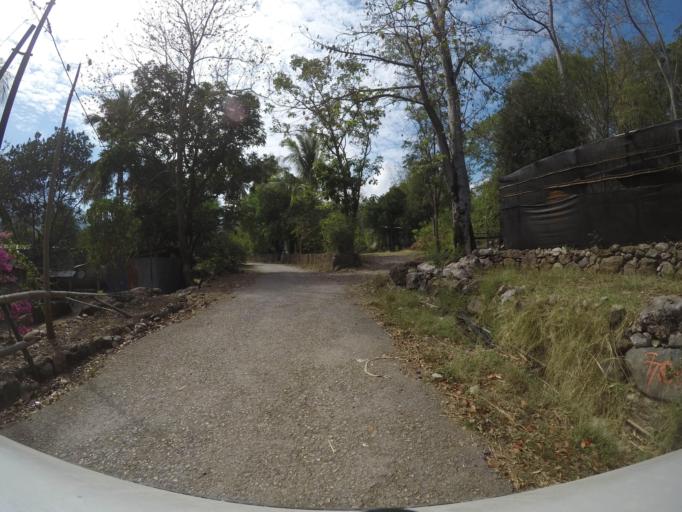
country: TL
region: Bobonaro
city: Maliana
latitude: -8.9946
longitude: 125.2254
